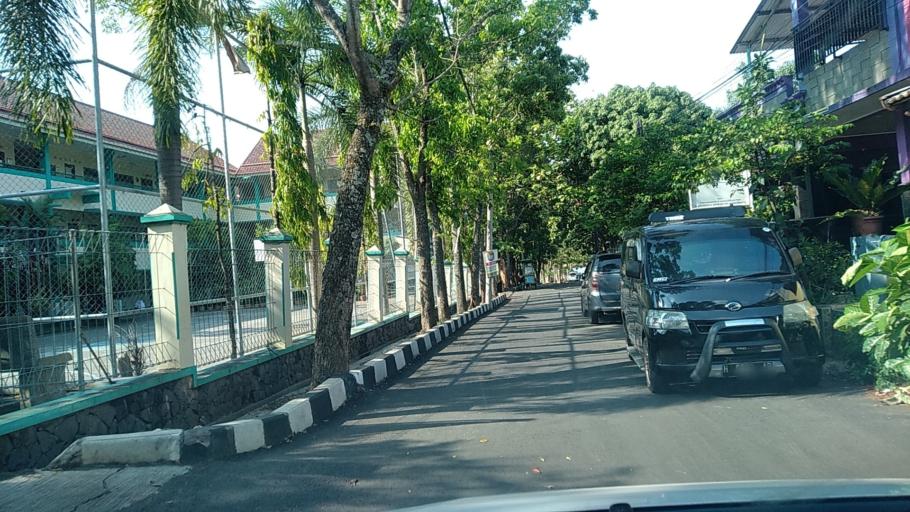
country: ID
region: Central Java
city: Semarang
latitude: -7.0576
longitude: 110.4274
